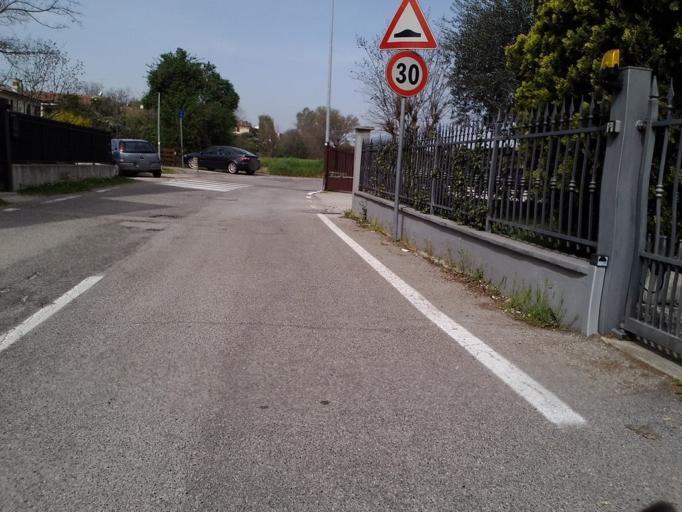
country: IT
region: Veneto
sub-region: Provincia di Verona
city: Sommacampagna
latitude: 45.4012
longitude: 10.8411
